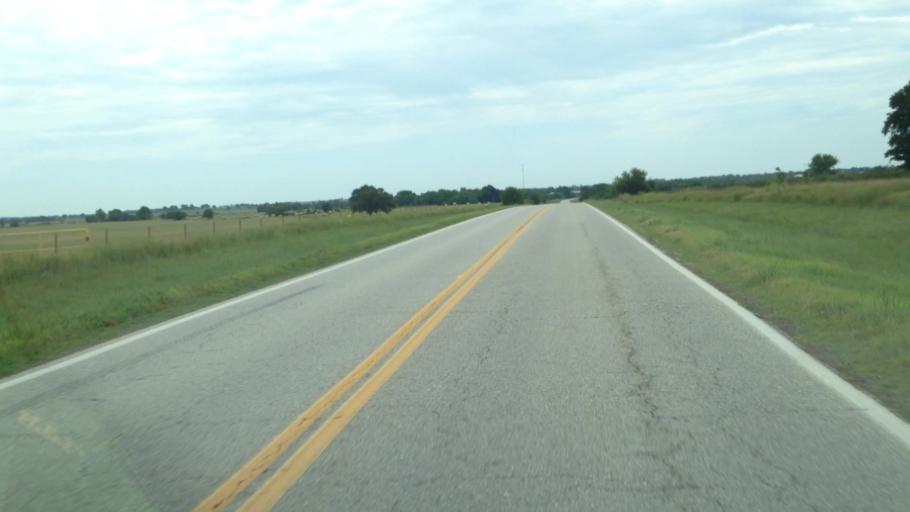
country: US
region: Kansas
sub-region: Labette County
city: Chetopa
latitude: 36.8543
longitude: -95.1180
